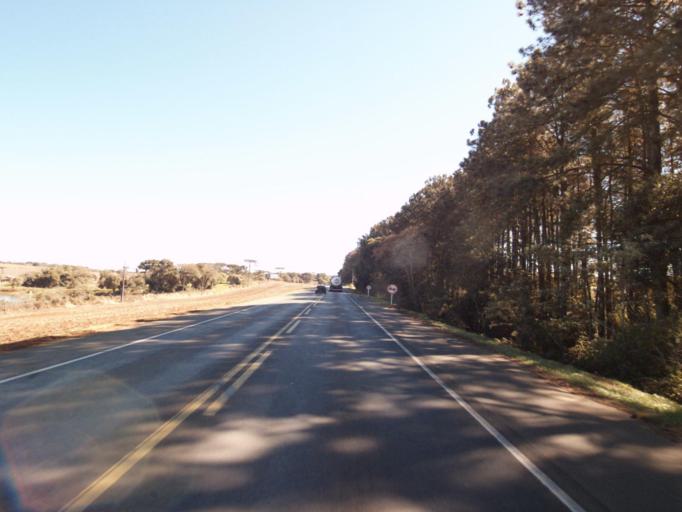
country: BR
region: Santa Catarina
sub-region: Xanxere
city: Xanxere
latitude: -26.8720
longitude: -52.2982
